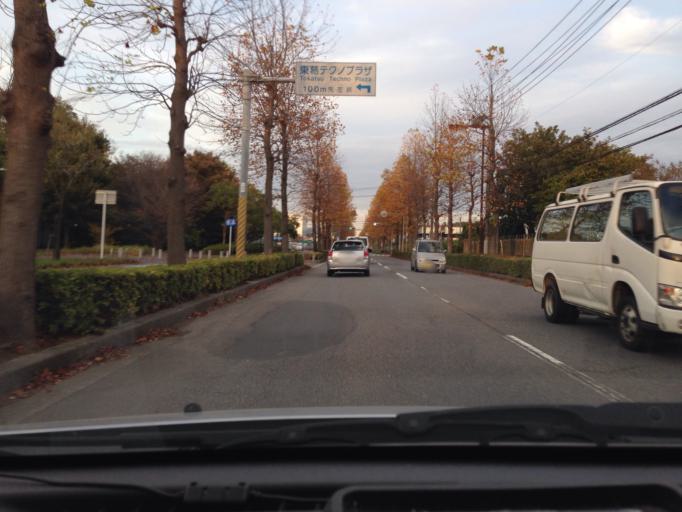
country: JP
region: Chiba
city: Kashiwa
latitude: 35.9013
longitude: 139.9398
